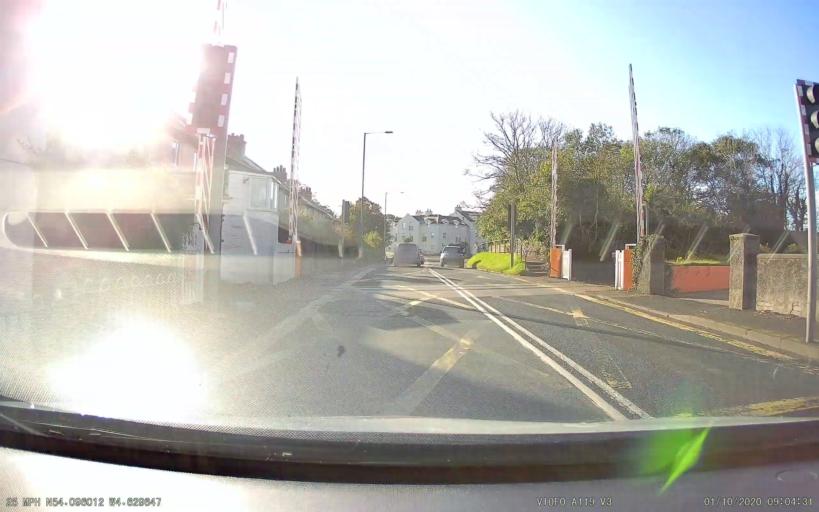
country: IM
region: Castletown
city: Castletown
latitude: 54.0960
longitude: -4.6296
